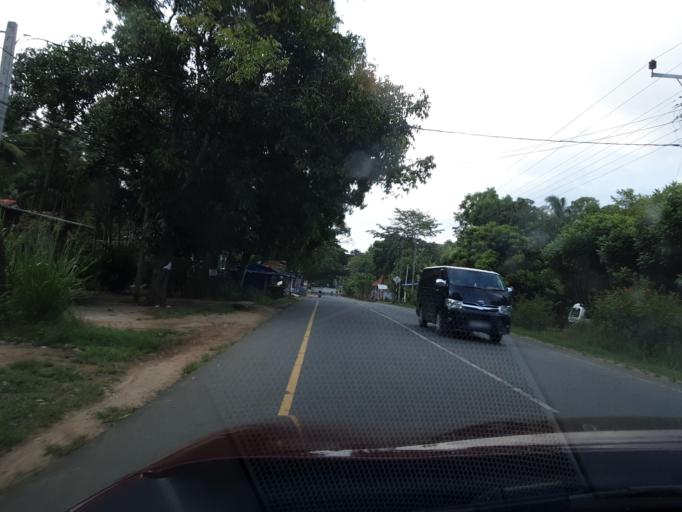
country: LK
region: Uva
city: Haputale
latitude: 6.6878
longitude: 81.1077
